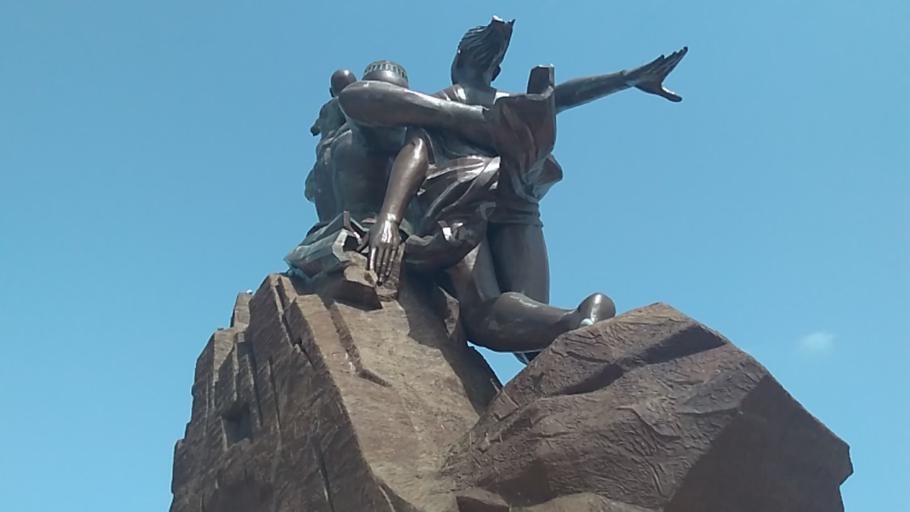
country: SN
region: Dakar
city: Mermoz Boabab
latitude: 14.7219
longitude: -17.4948
